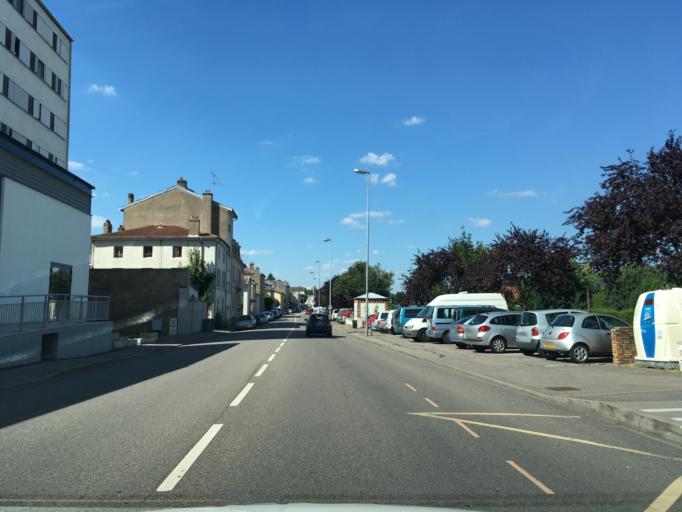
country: FR
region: Lorraine
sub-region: Departement de Meurthe-et-Moselle
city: Maxeville
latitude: 48.7091
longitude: 6.1670
